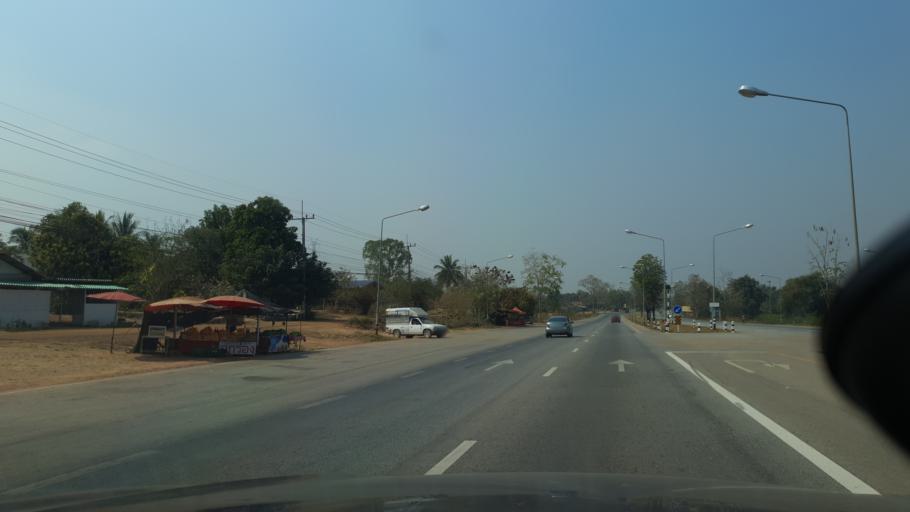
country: TH
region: Kamphaeng Phet
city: Kosamphi Nakhon
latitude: 16.6131
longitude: 99.3725
